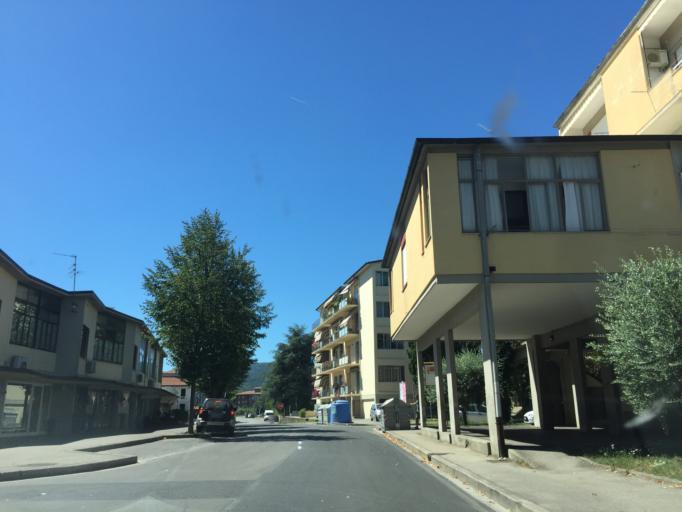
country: IT
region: Tuscany
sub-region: Provincia di Pistoia
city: Pistoia
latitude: 43.9489
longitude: 10.9060
